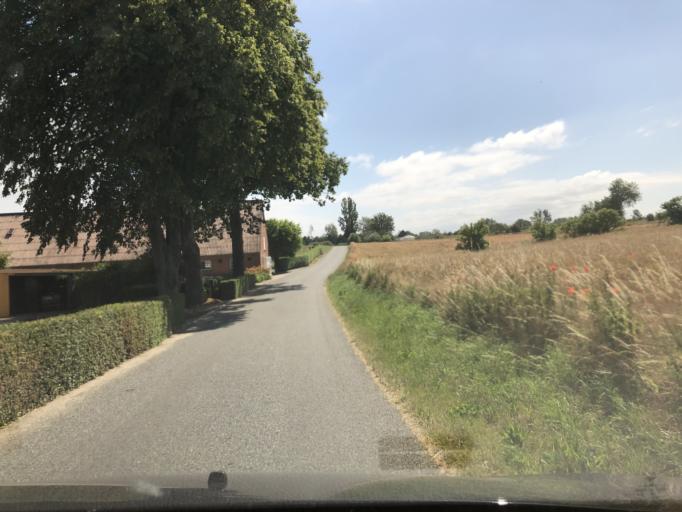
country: DK
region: South Denmark
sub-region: AEro Kommune
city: AEroskobing
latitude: 54.9287
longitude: 10.2862
